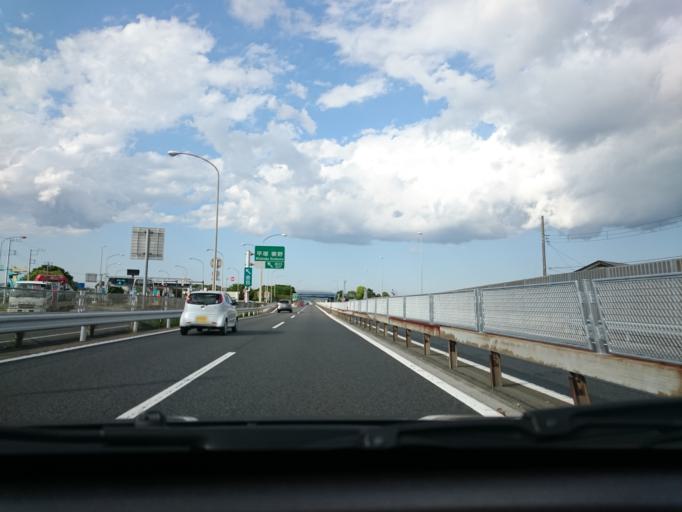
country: JP
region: Kanagawa
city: Isehara
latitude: 35.3611
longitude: 139.3045
